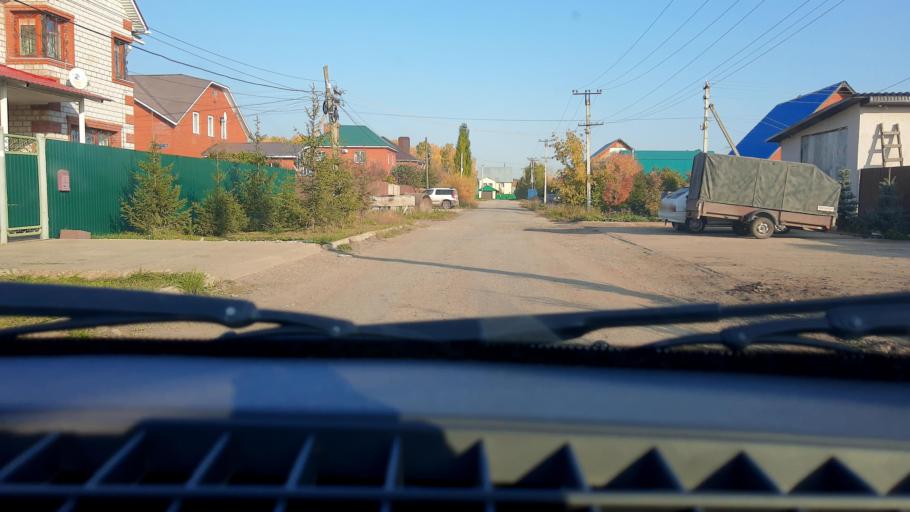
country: RU
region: Bashkortostan
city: Ufa
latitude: 54.6512
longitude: 55.9270
